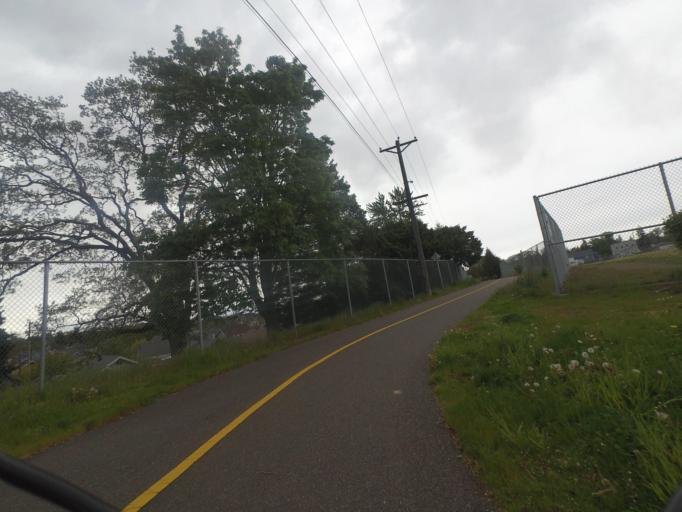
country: US
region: Washington
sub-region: Pierce County
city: Lakewood
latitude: 47.2031
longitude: -122.4766
